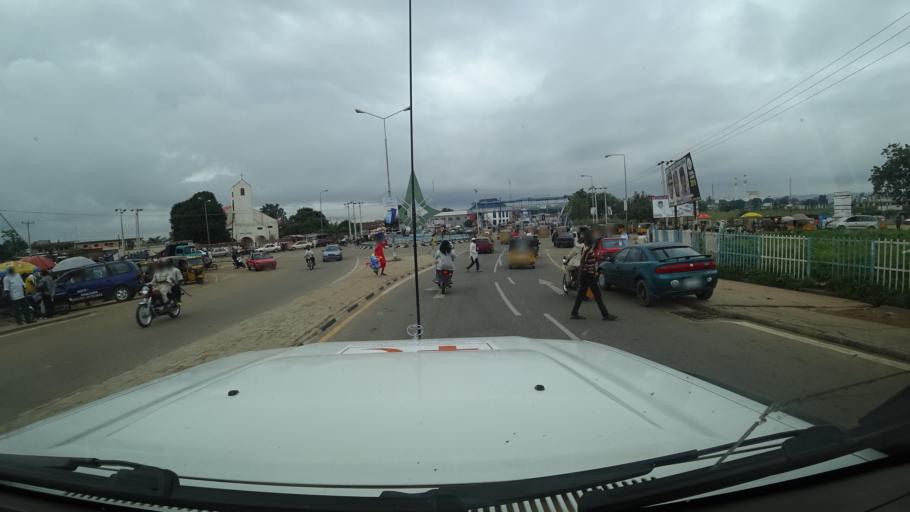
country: NG
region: Niger
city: Minna
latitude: 9.6140
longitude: 6.5478
